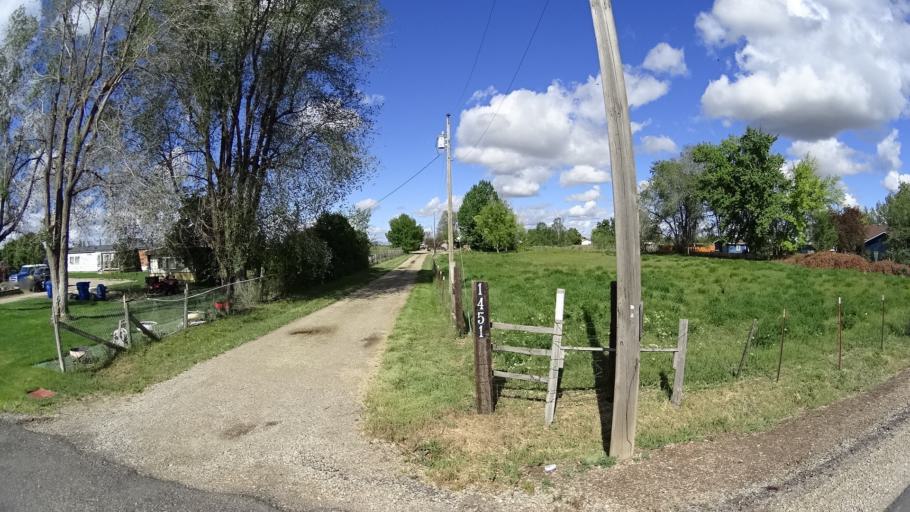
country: US
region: Idaho
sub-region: Ada County
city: Kuna
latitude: 43.5016
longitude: -116.4537
